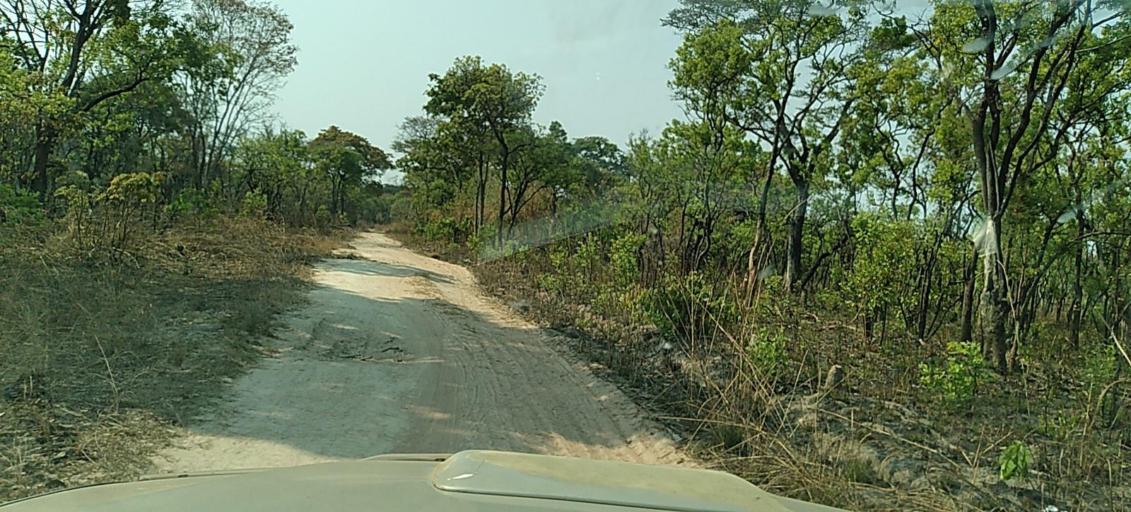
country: ZM
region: North-Western
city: Kasempa
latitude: -13.5383
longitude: 26.4087
